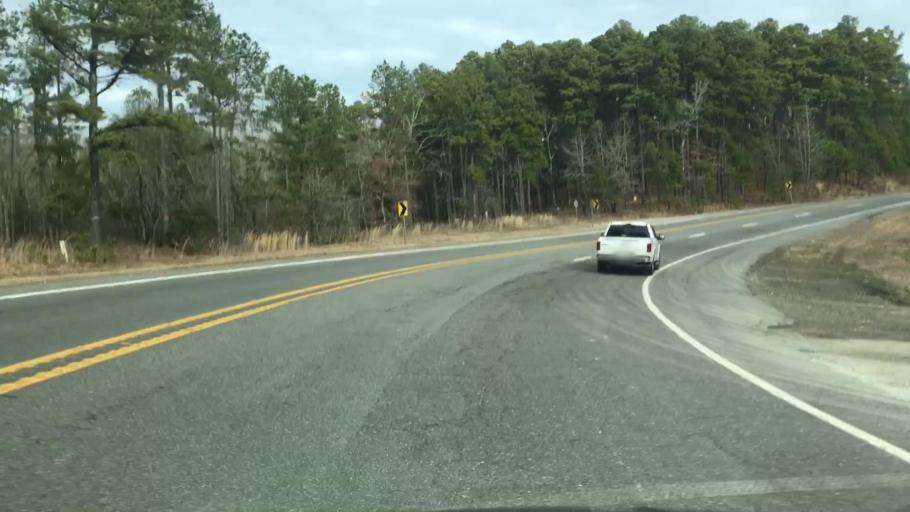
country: US
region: Arkansas
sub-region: Montgomery County
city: Mount Ida
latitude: 34.5930
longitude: -93.6661
